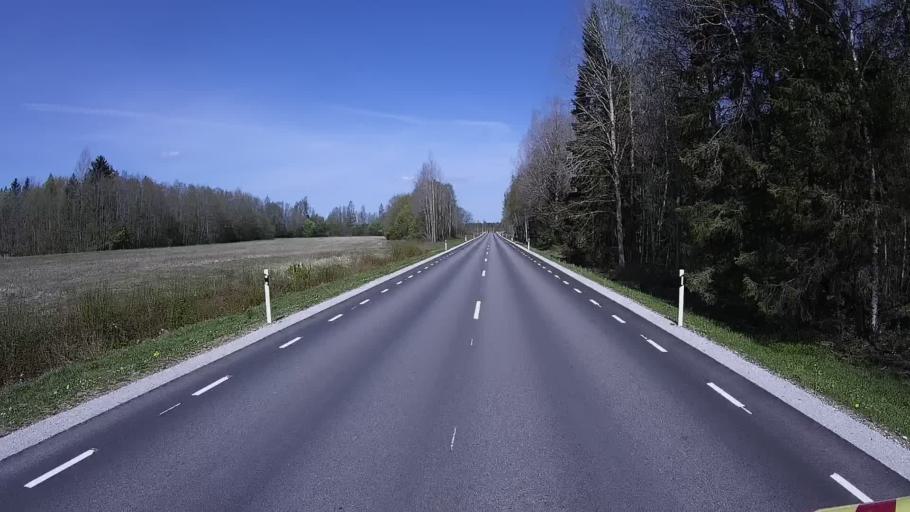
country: EE
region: Harju
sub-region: Nissi vald
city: Turba
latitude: 59.1651
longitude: 24.0742
